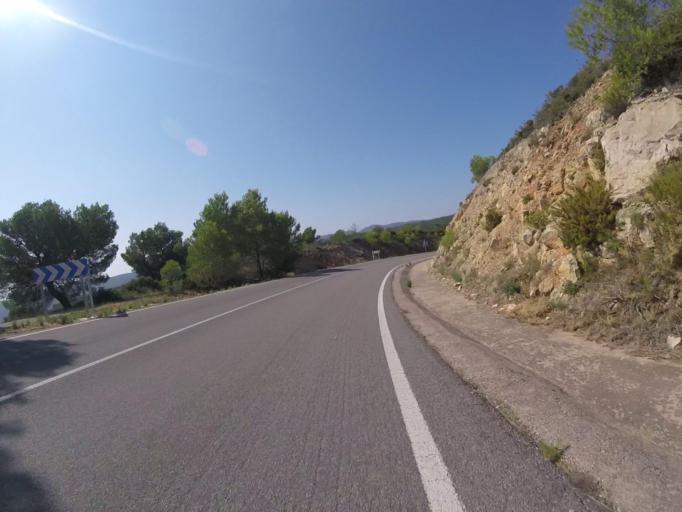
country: ES
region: Valencia
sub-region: Provincia de Castello
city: Adzaneta
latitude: 40.2392
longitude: -0.1880
